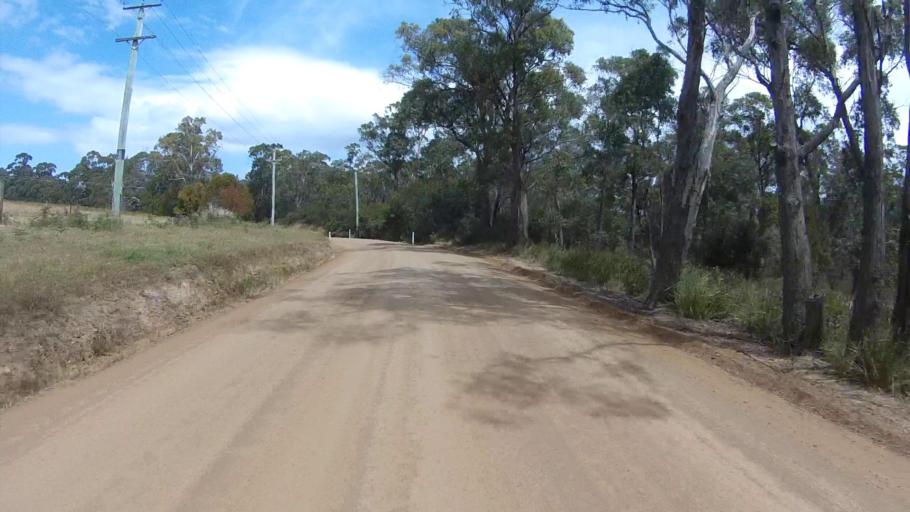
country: AU
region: Tasmania
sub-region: Kingborough
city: Blackmans Bay
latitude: -43.0434
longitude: 147.3059
